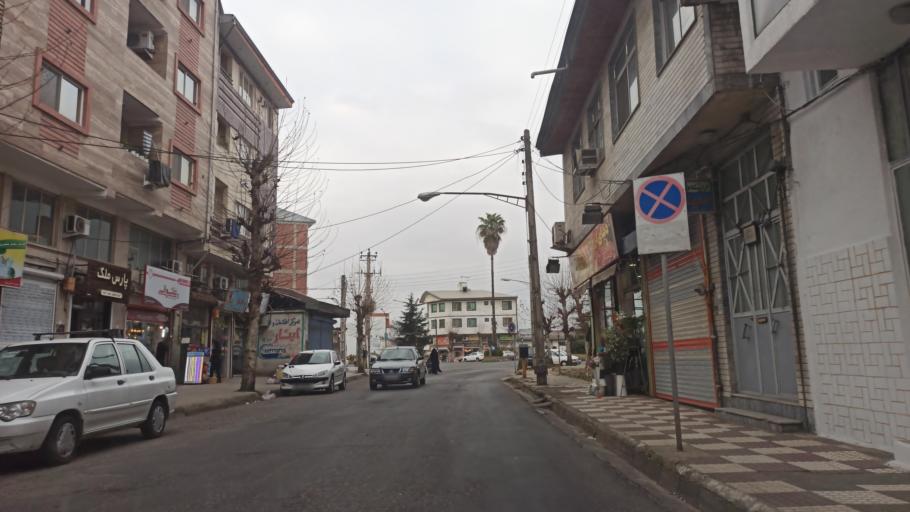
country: IR
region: Gilan
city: Fuman
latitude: 37.2301
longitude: 49.3155
